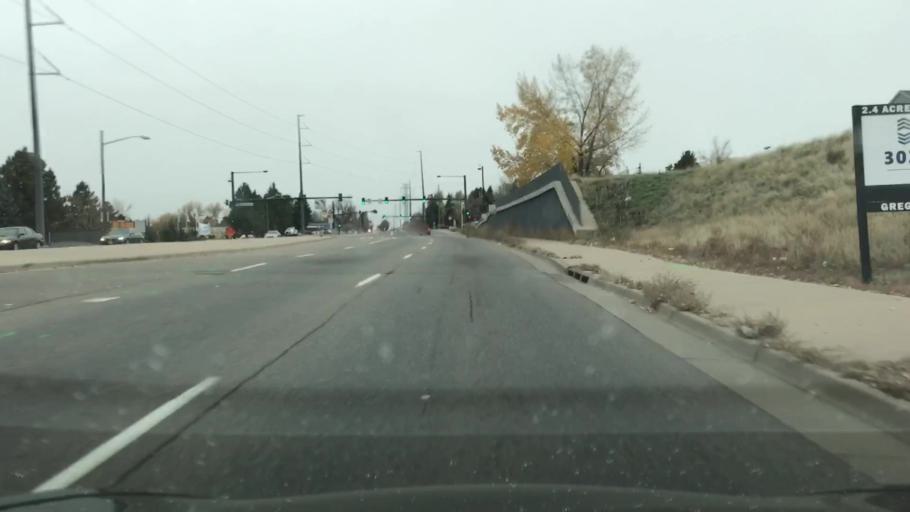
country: US
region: Colorado
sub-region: Arapahoe County
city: Glendale
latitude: 39.6793
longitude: -104.9036
